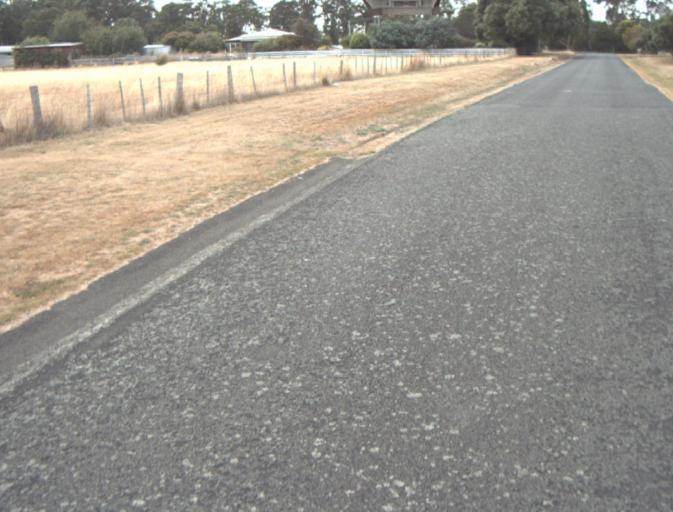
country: AU
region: Tasmania
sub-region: Launceston
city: Mayfield
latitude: -41.3273
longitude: 147.0575
